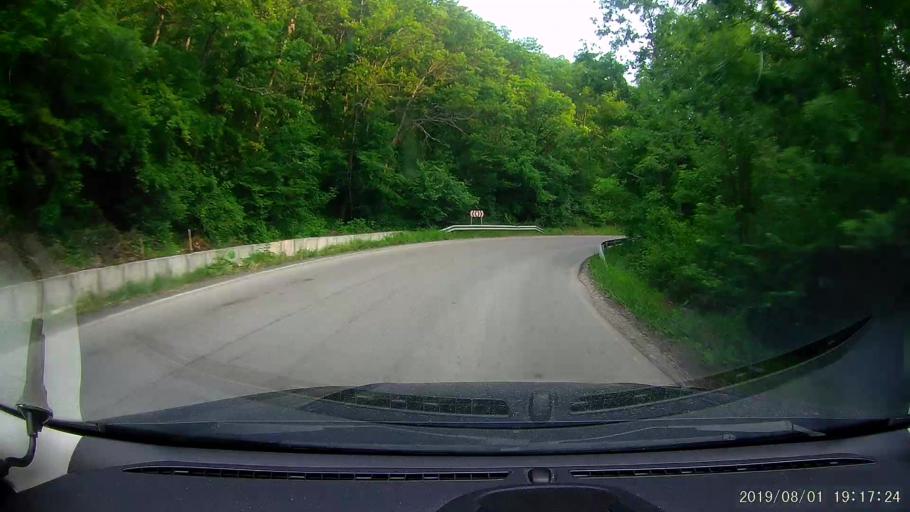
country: BG
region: Shumen
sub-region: Obshtina Smyadovo
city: Smyadovo
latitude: 42.9238
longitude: 26.9429
